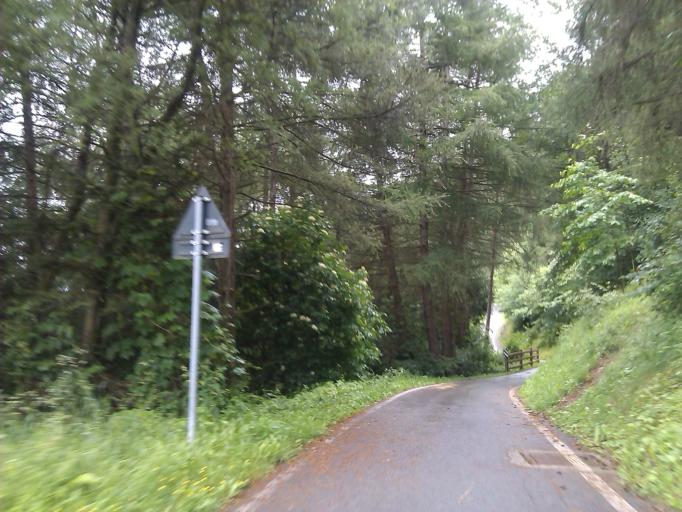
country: IT
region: Trentino-Alto Adige
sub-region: Bolzano
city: Lasa
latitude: 46.6107
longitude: 10.7104
